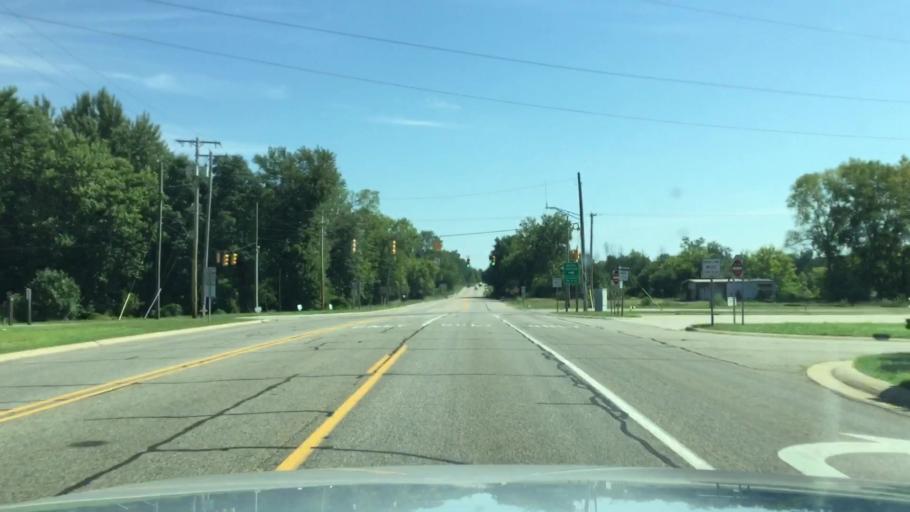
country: US
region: Michigan
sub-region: Jackson County
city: Brooklyn
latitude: 42.0590
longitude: -84.2216
